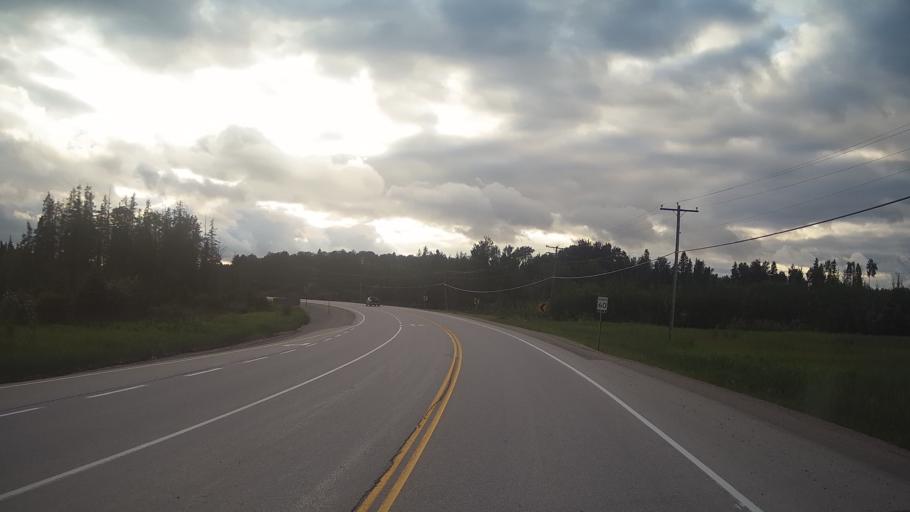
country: CA
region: Ontario
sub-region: Rainy River District
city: Atikokan
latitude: 49.0502
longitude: -90.4719
